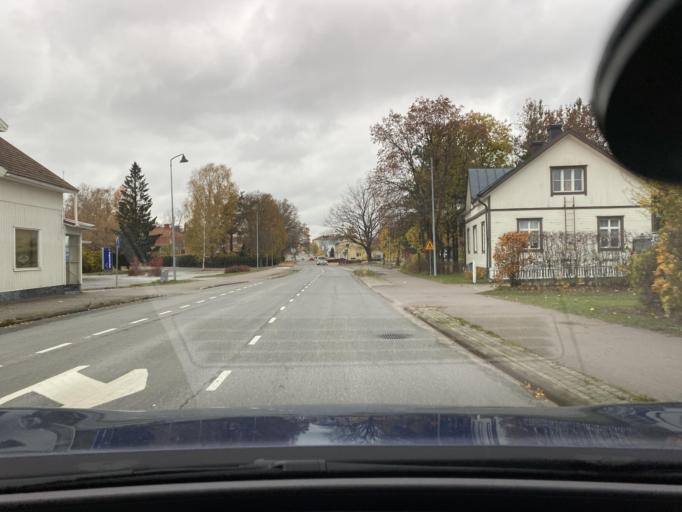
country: FI
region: Varsinais-Suomi
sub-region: Vakka-Suomi
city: Laitila
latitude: 60.8768
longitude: 21.6990
